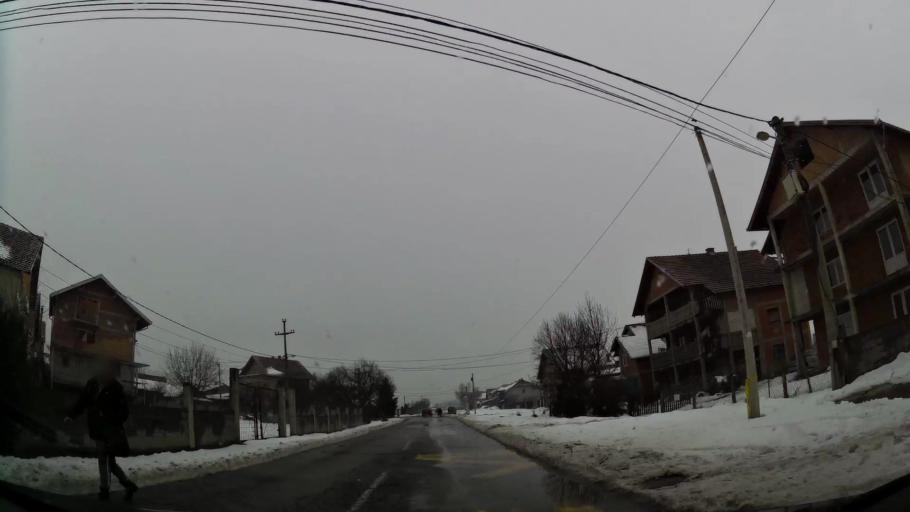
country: RS
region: Central Serbia
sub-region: Belgrade
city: Zemun
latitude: 44.8577
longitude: 20.3297
